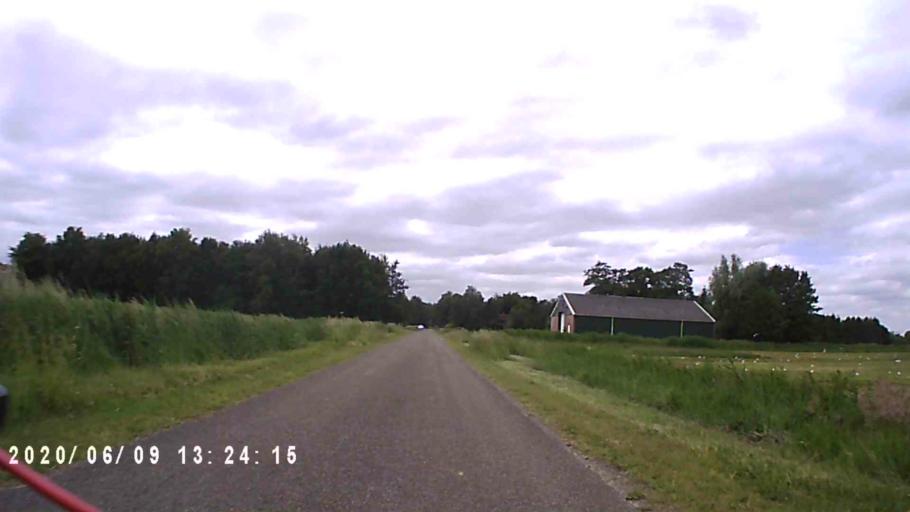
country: NL
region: Groningen
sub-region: Gemeente Haren
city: Haren
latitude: 53.2229
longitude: 6.6811
